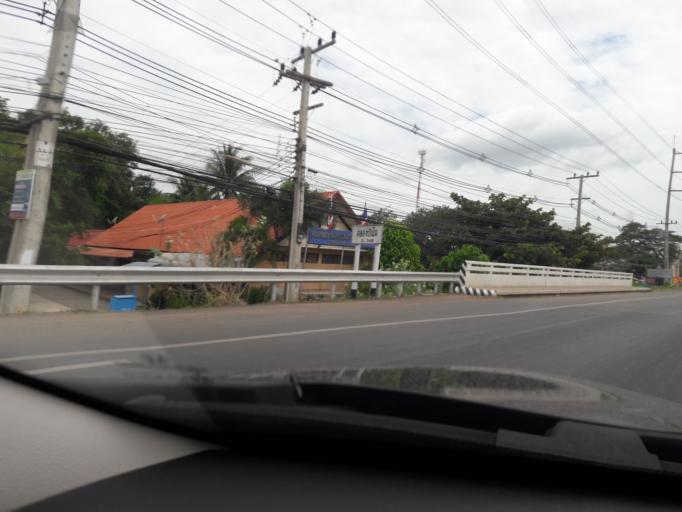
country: TH
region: Ratchaburi
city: Damnoen Saduak
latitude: 13.5522
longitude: 99.9675
